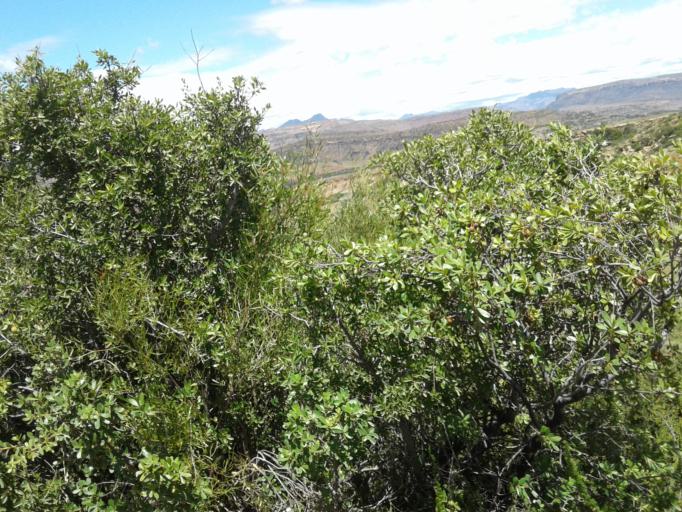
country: LS
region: Quthing
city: Quthing
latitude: -30.3781
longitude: 27.5580
